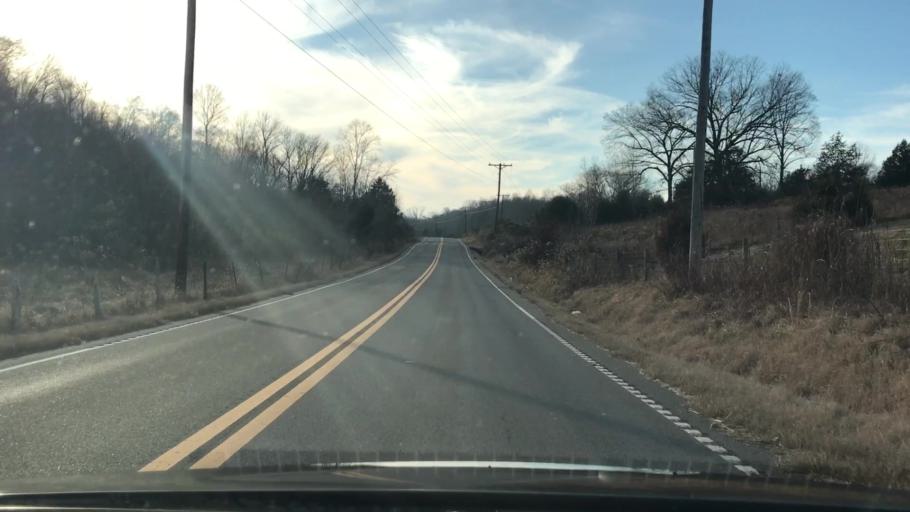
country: US
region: Tennessee
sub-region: Macon County
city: Red Boiling Springs
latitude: 36.6178
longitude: -85.7938
